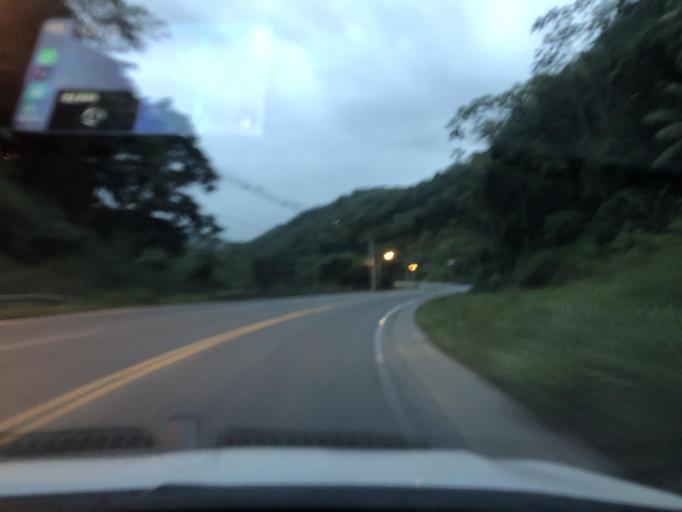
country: BR
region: Santa Catarina
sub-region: Pomerode
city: Pomerode
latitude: -26.7201
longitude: -49.0605
